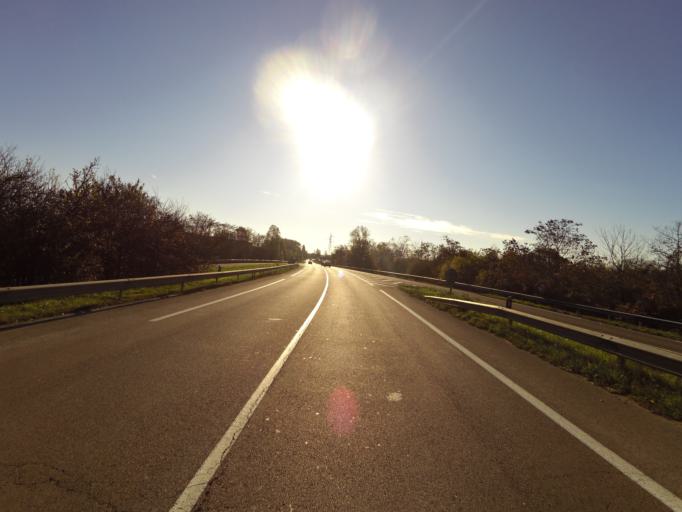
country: FR
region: Champagne-Ardenne
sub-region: Departement de l'Aube
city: Bucheres
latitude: 48.2324
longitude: 4.1248
